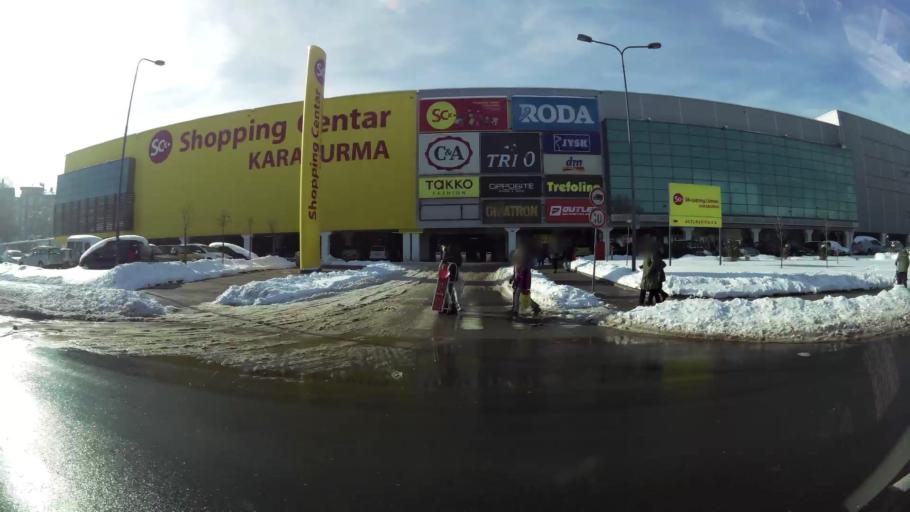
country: RS
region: Central Serbia
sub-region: Belgrade
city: Palilula
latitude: 44.8115
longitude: 20.5227
